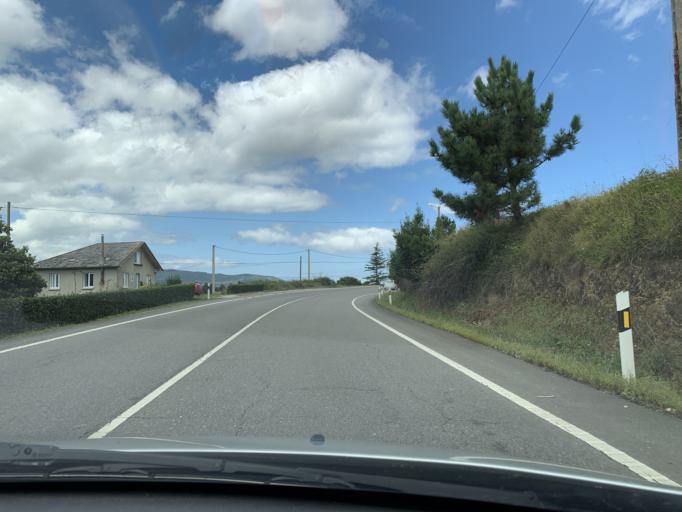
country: ES
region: Galicia
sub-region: Provincia de Lugo
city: Barreiros
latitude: 43.5227
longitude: -7.2684
